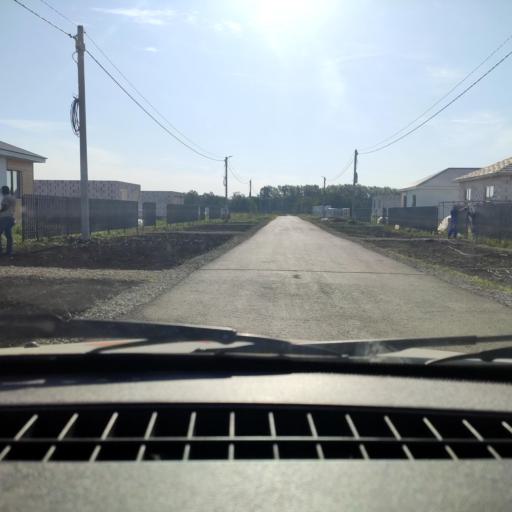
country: RU
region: Bashkortostan
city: Kabakovo
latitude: 54.6289
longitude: 56.1384
